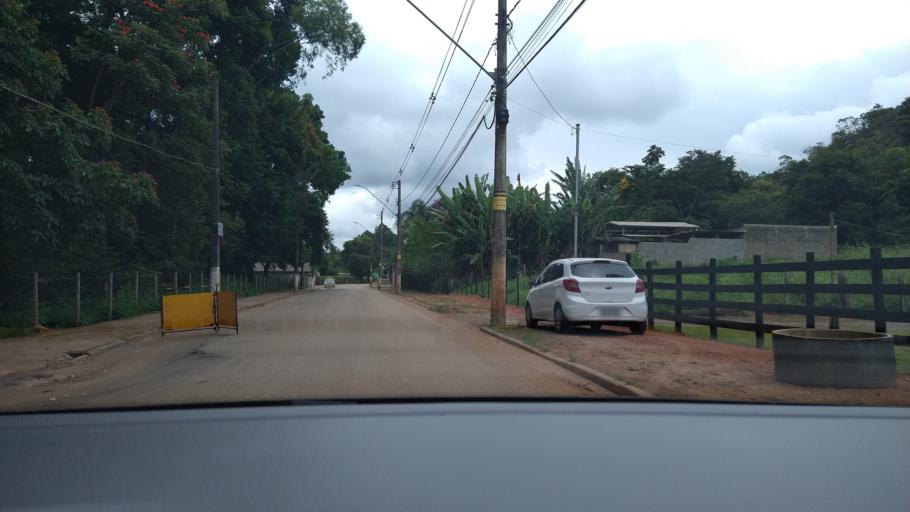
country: BR
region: Minas Gerais
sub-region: Rio Piracicaba
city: Rio Piracicaba
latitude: -19.9383
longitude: -43.1801
